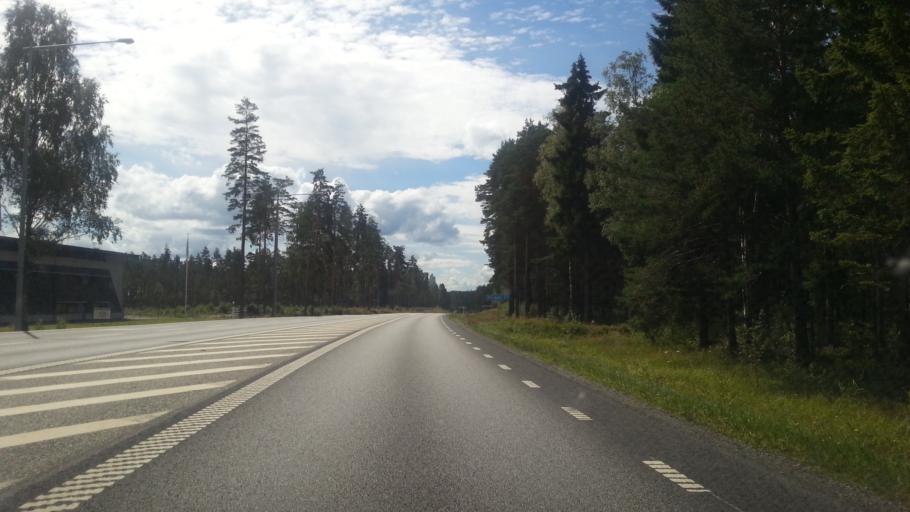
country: SE
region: OErebro
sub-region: Lindesbergs Kommun
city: Lindesberg
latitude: 59.6168
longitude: 15.1887
